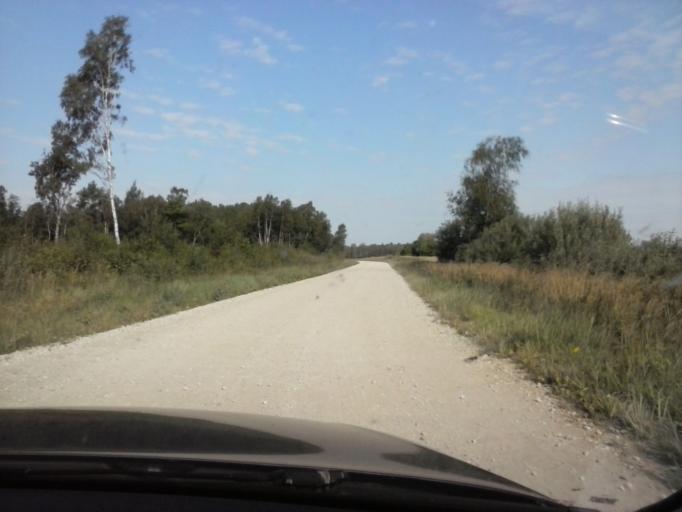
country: EE
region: Laeaene
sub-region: Ridala Parish
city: Uuemoisa
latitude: 58.8821
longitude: 23.5845
